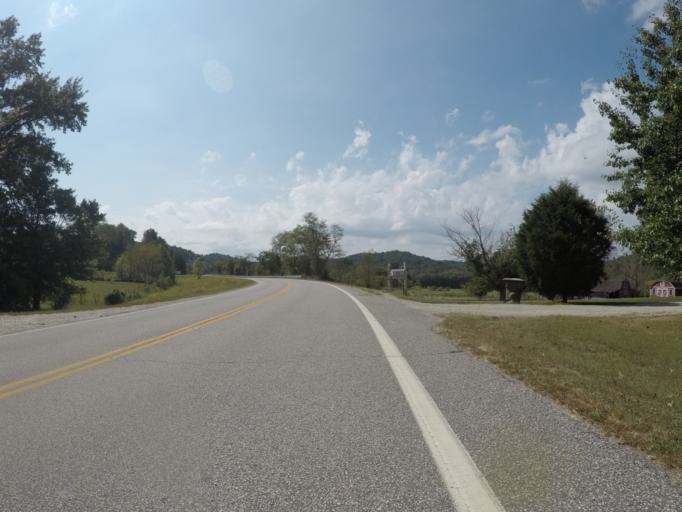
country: US
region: West Virginia
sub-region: Cabell County
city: Lesage
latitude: 38.5137
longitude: -82.3922
